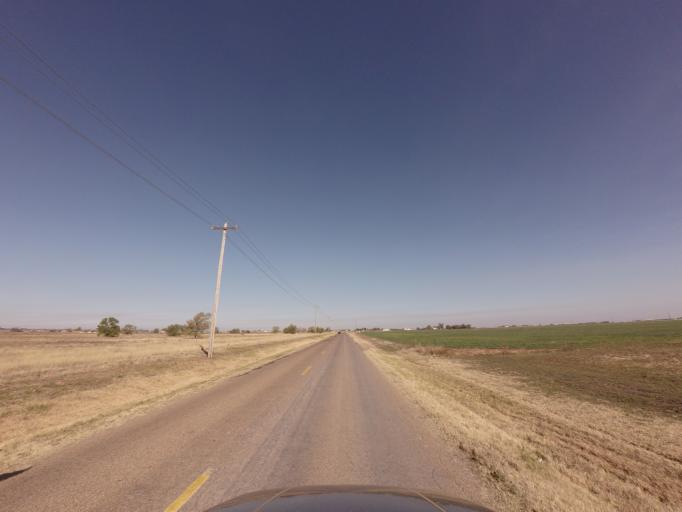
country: US
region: New Mexico
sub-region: Curry County
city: Clovis
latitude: 34.4065
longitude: -103.1612
